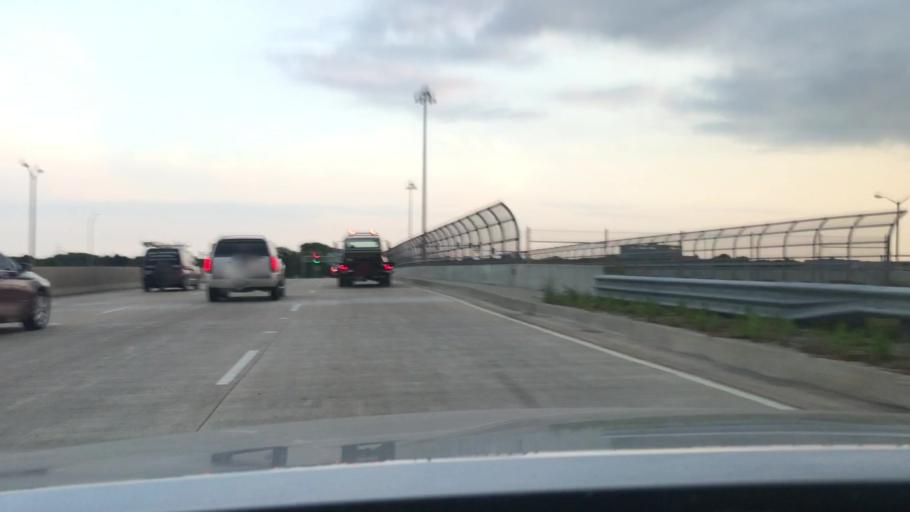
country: US
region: Illinois
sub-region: DuPage County
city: Warrenville
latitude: 41.8043
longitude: -88.2036
